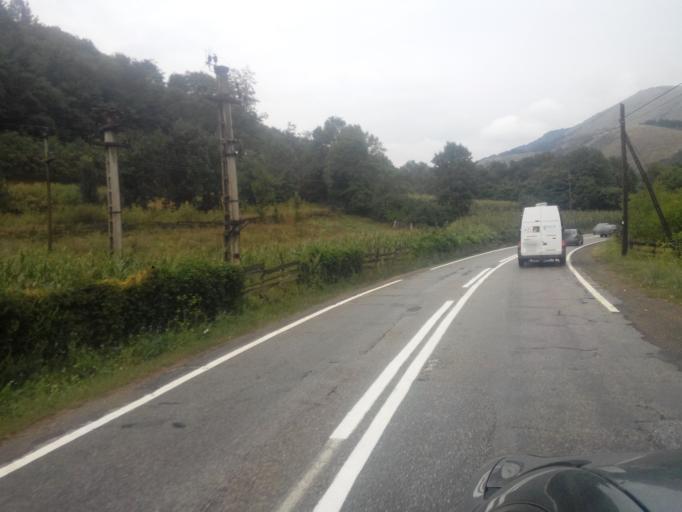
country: RO
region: Alba
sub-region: Comuna Ocolis
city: Ocolis
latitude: 46.4644
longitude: 23.4730
